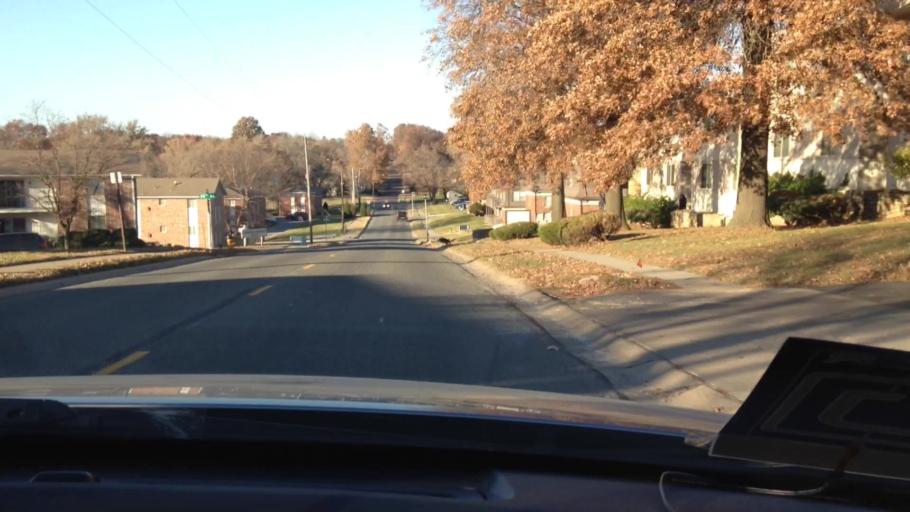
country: US
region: Kansas
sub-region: Johnson County
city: Overland Park
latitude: 38.9688
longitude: -94.6630
